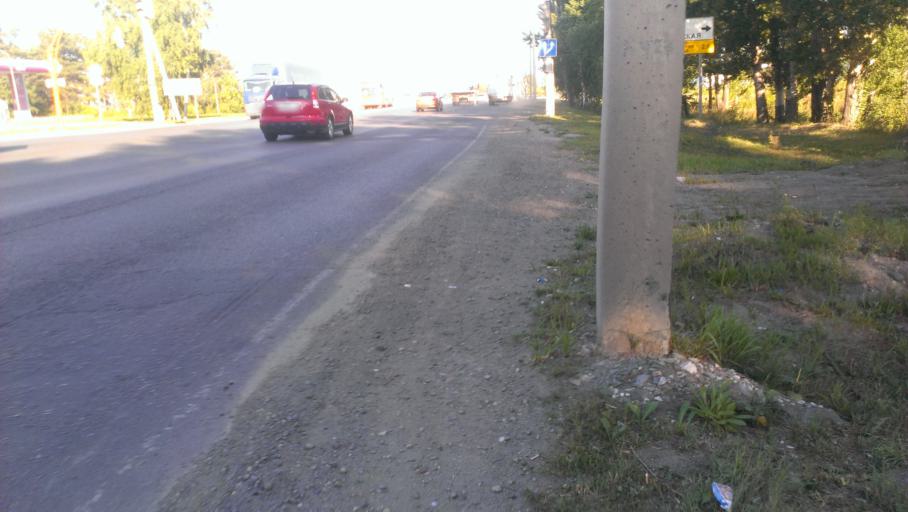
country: RU
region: Altai Krai
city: Novosilikatnyy
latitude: 53.3484
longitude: 83.6280
